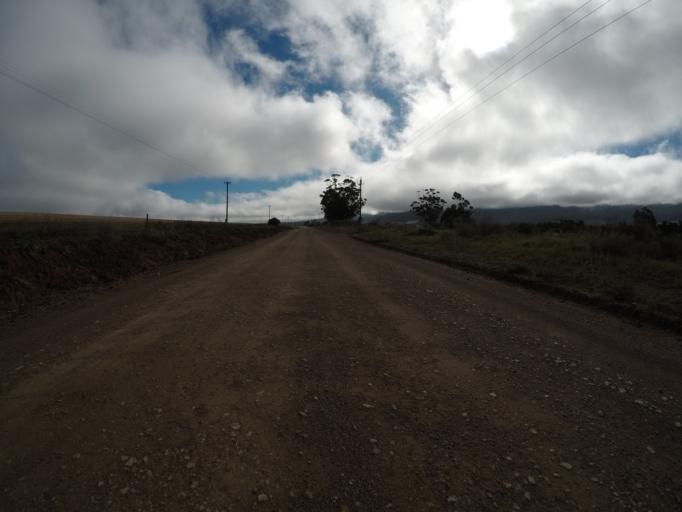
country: ZA
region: Western Cape
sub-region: Cape Winelands District Municipality
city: Ashton
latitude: -34.1353
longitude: 19.8579
